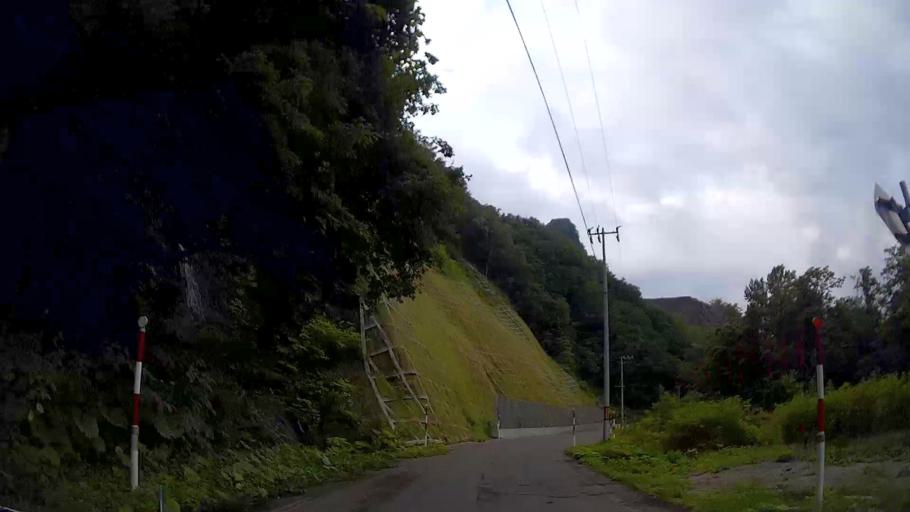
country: JP
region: Hokkaido
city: Nanae
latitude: 42.0731
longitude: 140.5222
